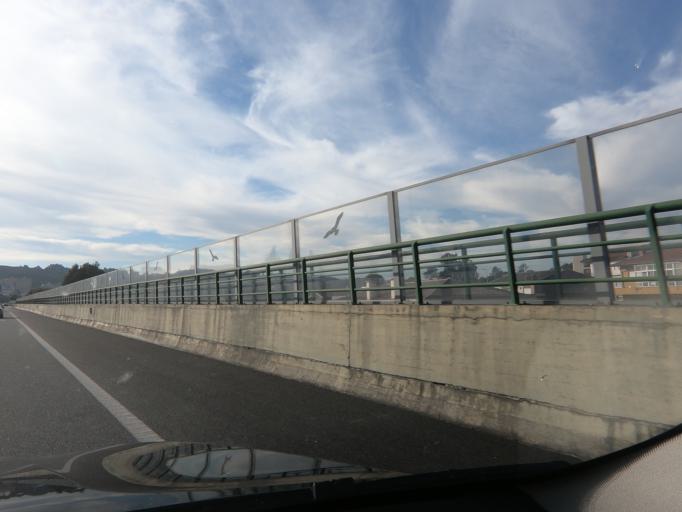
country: PT
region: Porto
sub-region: Valongo
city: Valongo
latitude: 41.1976
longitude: -8.5014
